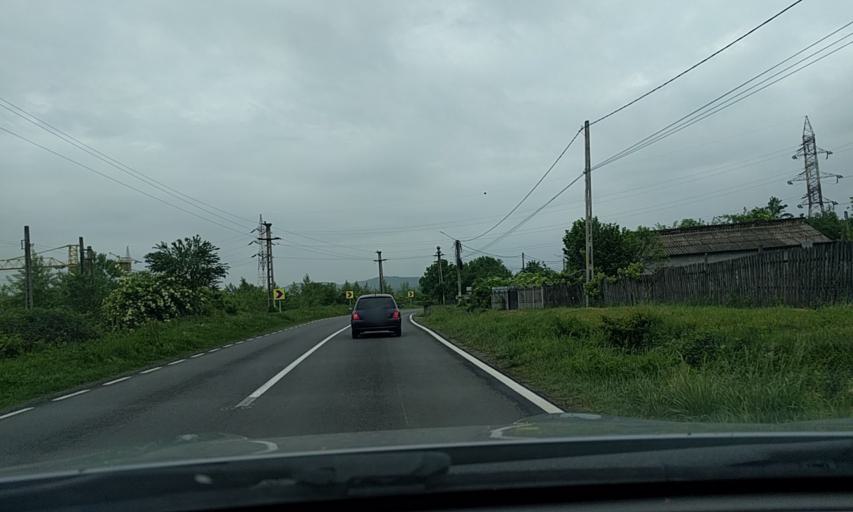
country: RO
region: Dambovita
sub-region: Comuna Vulcana-Pandele
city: Vulcana-Pandele
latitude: 45.0073
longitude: 25.4014
